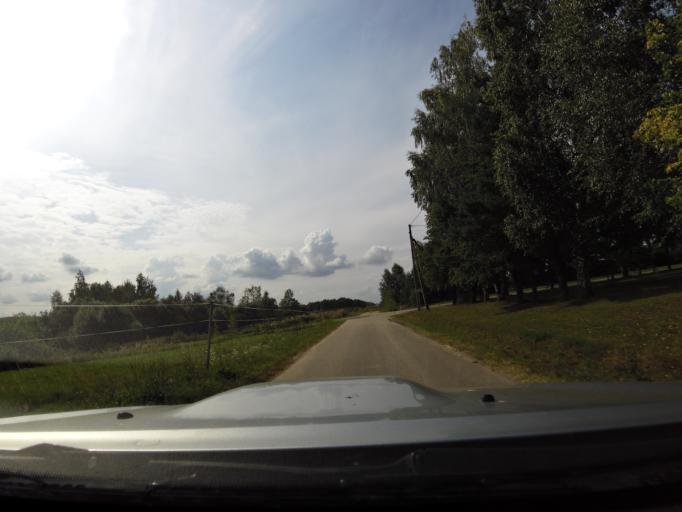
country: LT
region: Vilnius County
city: Elektrenai
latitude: 54.8612
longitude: 24.5740
